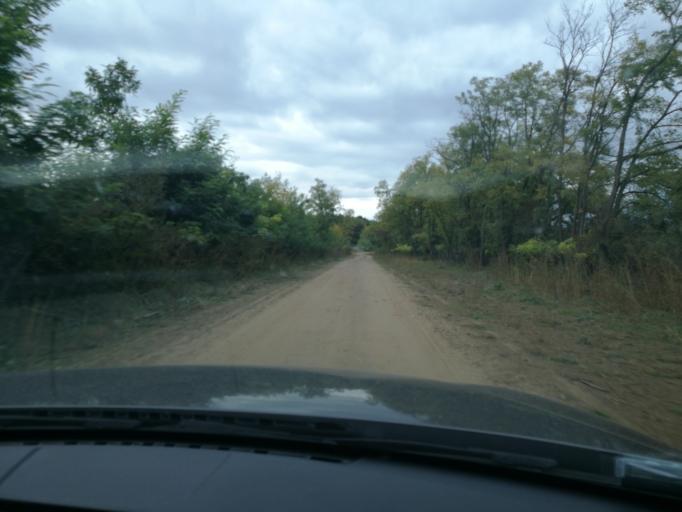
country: HU
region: Szabolcs-Szatmar-Bereg
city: Nyirpazony
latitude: 47.9939
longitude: 21.7882
